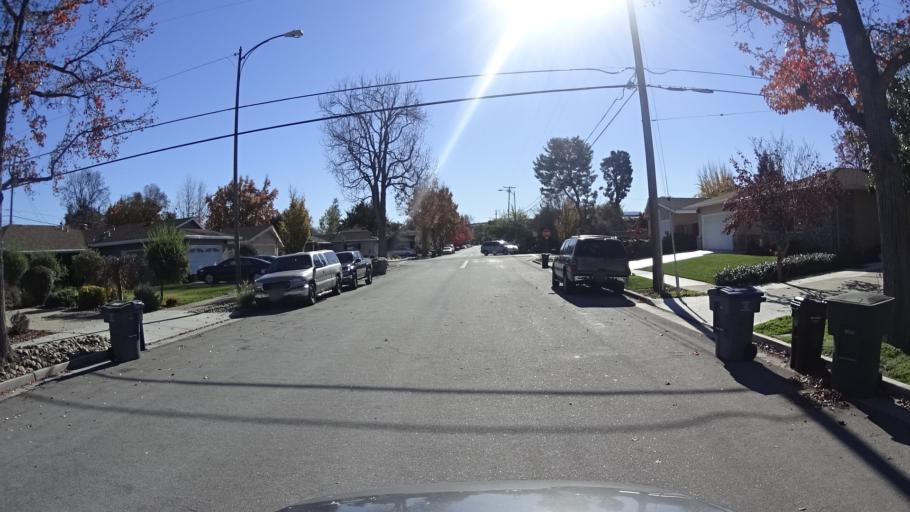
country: US
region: California
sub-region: Santa Clara County
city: Cupertino
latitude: 37.3421
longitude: -122.0073
